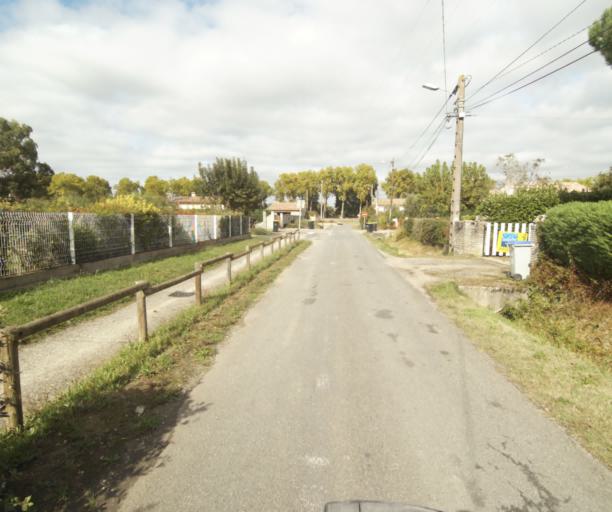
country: FR
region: Midi-Pyrenees
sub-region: Departement du Tarn-et-Garonne
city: Montech
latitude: 43.9540
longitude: 1.2237
